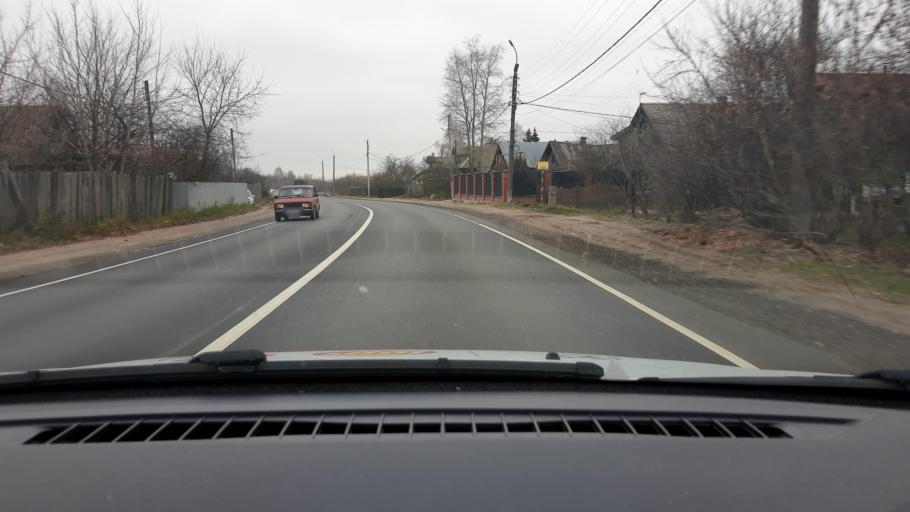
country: RU
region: Nizjnij Novgorod
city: Gidrotorf
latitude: 56.5380
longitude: 43.5363
